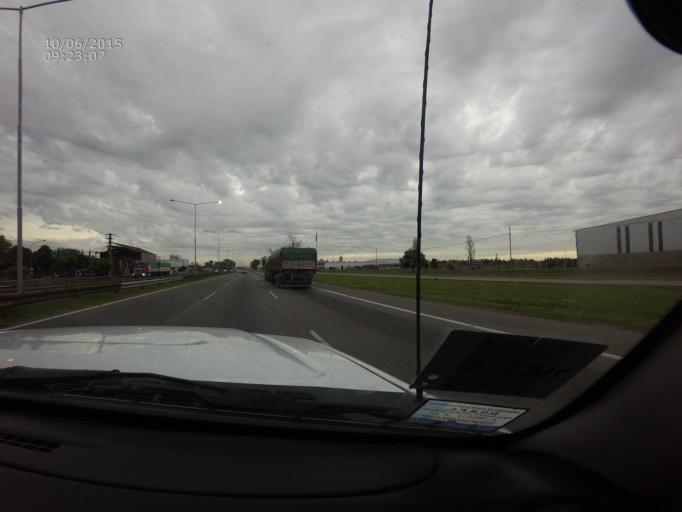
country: AR
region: Buenos Aires
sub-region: Partido de Campana
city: Campana
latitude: -34.2094
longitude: -58.9304
